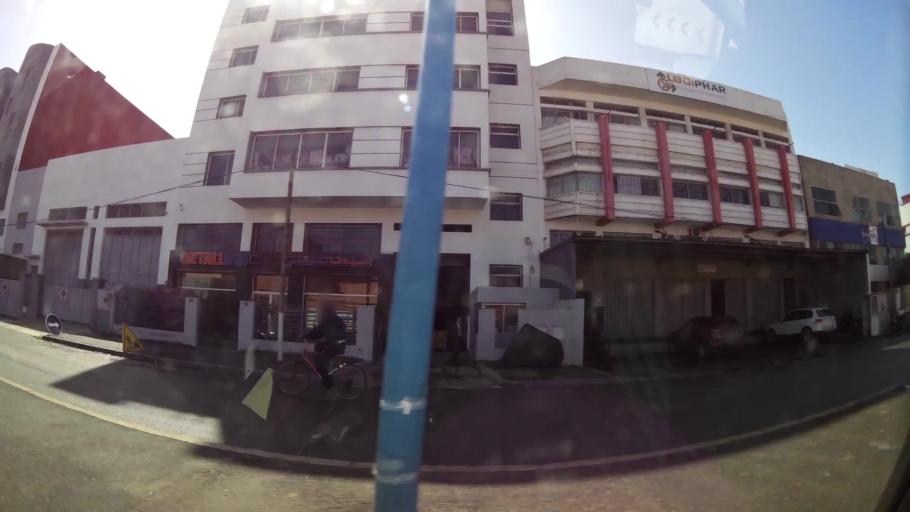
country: MA
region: Grand Casablanca
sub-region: Mediouna
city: Tit Mellil
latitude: 33.6207
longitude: -7.5076
